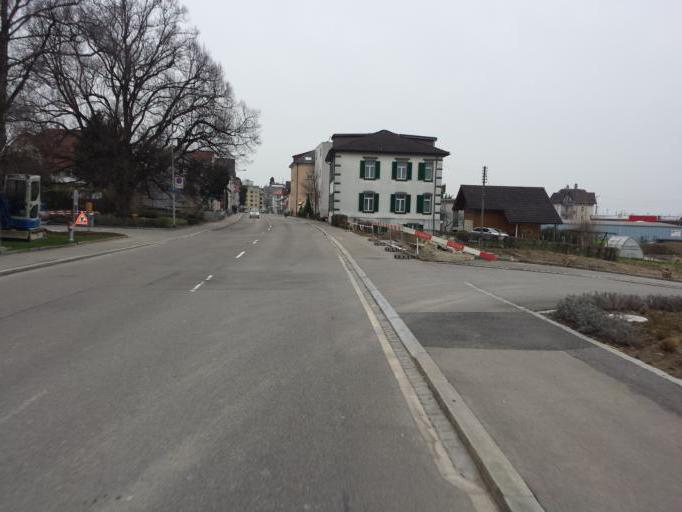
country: CH
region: Thurgau
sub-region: Arbon District
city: Salmsach
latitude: 47.5598
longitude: 9.3734
